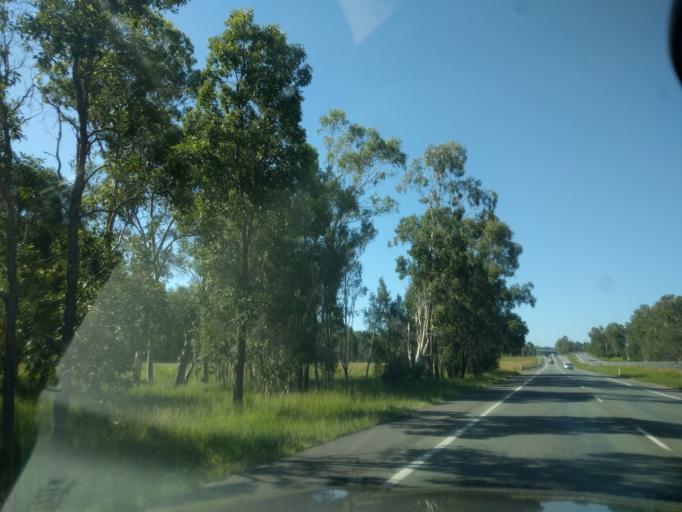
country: AU
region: Queensland
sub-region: Logan
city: Park Ridge South
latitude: -27.7321
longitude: 153.0287
